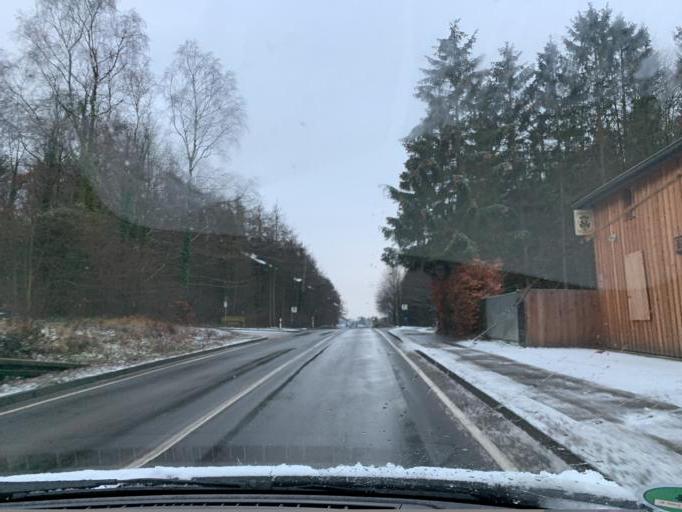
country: DE
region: North Rhine-Westphalia
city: Stolberg
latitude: 50.7445
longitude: 6.2486
